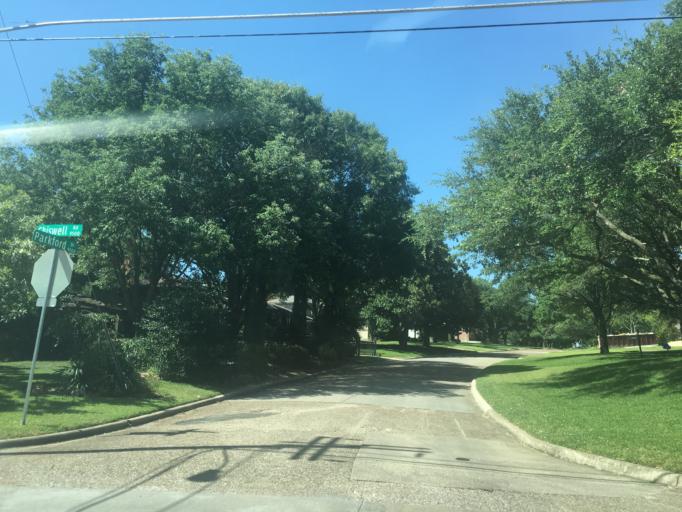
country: US
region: Texas
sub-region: Dallas County
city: Richardson
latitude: 32.8712
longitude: -96.7210
